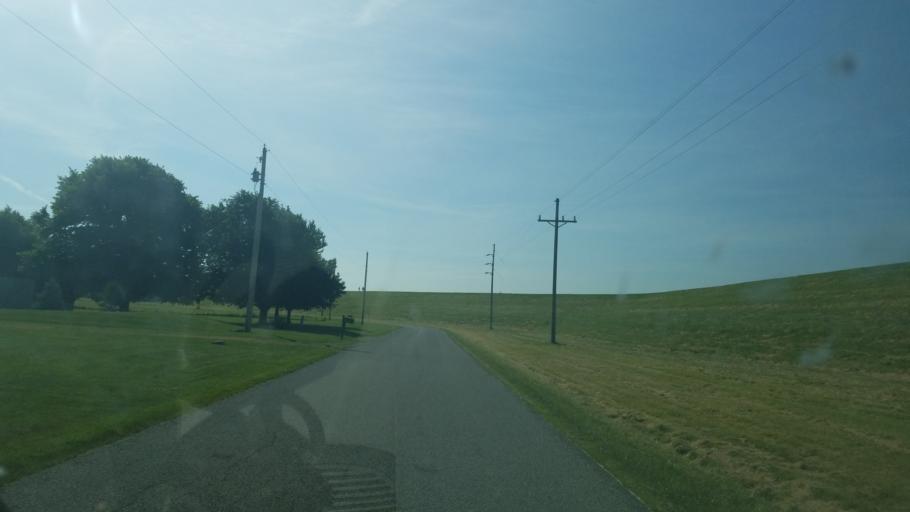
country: US
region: Ohio
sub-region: Hancock County
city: Findlay
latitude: 41.0281
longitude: -83.5653
